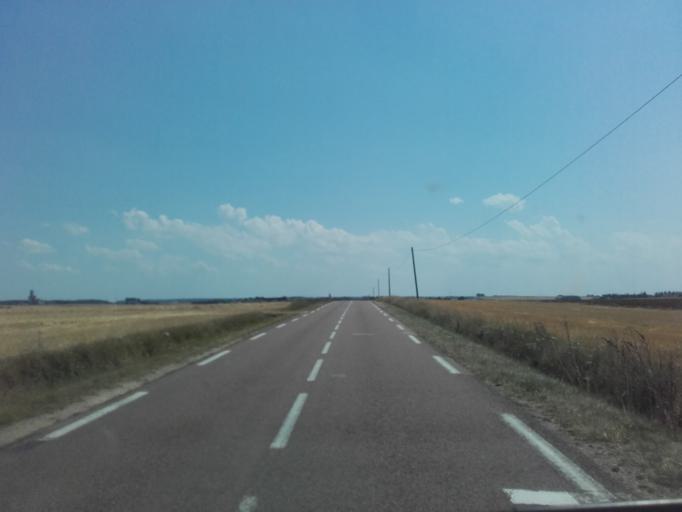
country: FR
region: Bourgogne
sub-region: Departement de l'Yonne
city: Joux-la-Ville
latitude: 47.6884
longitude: 3.8670
